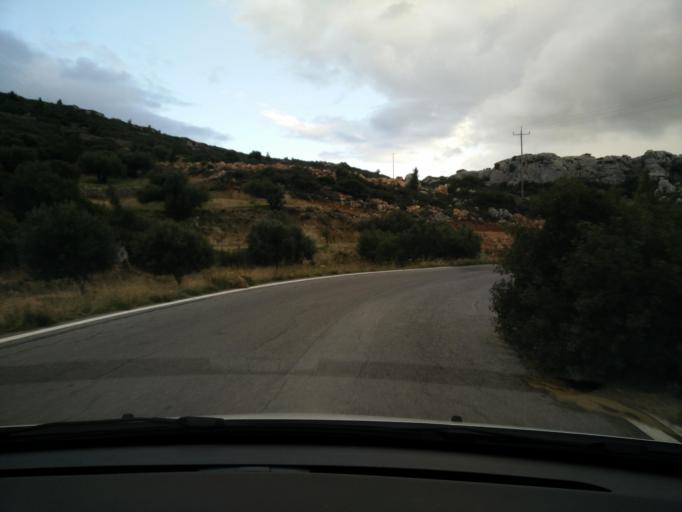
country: GR
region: Crete
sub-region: Nomos Lasithiou
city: Gra Liyia
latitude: 35.0747
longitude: 25.7040
